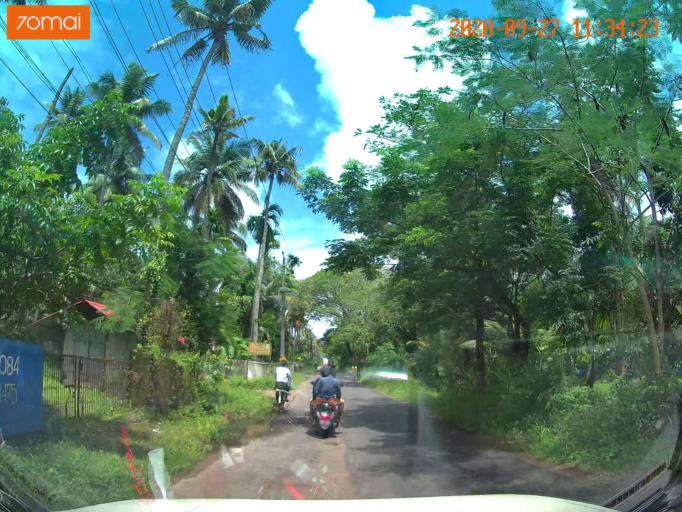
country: IN
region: Kerala
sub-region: Thrissur District
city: Thanniyam
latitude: 10.4365
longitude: 76.1268
